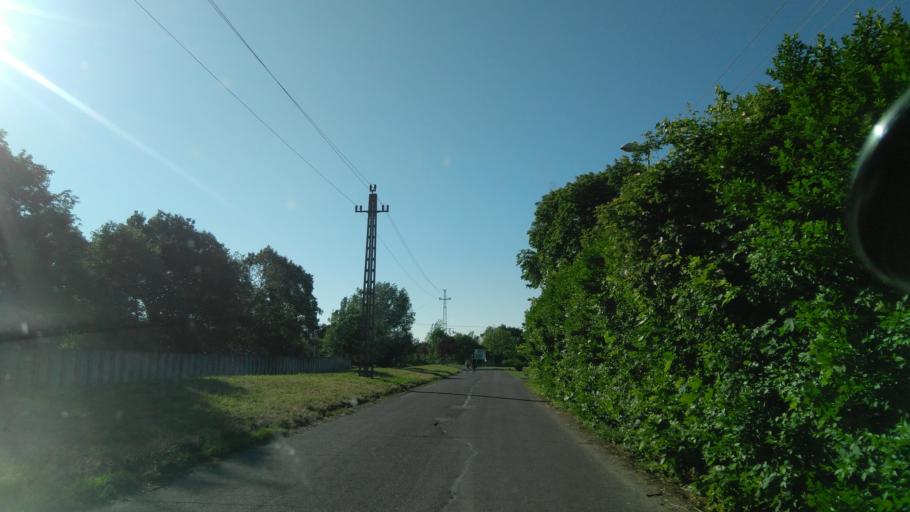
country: HU
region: Bekes
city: Gyula
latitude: 46.6366
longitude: 21.2581
